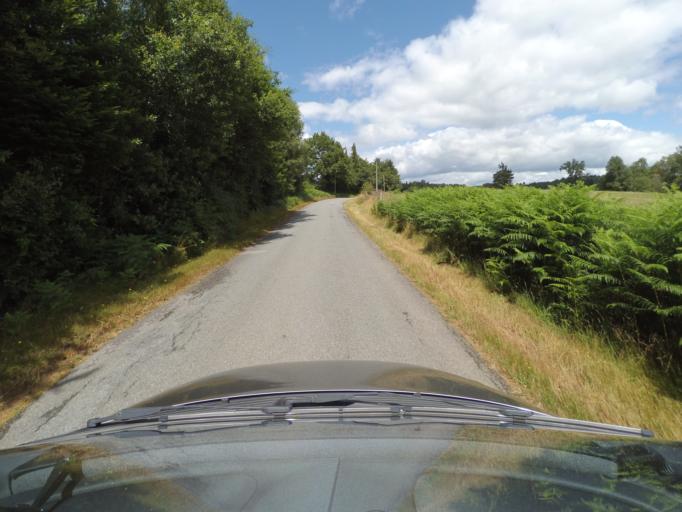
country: FR
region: Limousin
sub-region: Departement de la Creuse
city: Banize
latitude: 45.7807
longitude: 1.9384
